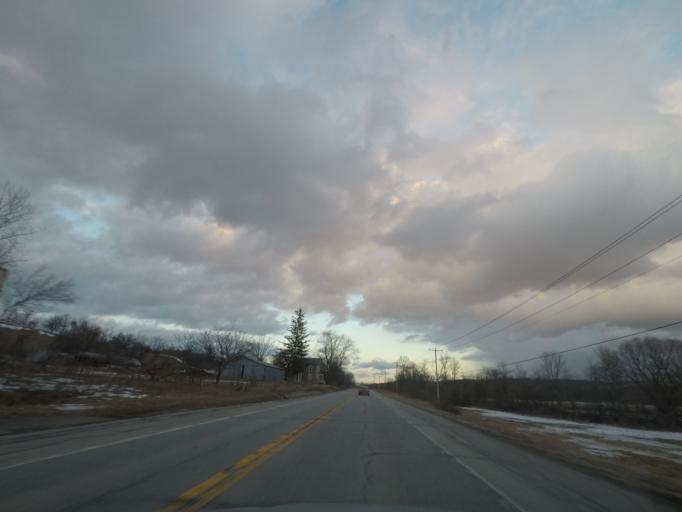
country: US
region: New York
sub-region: Montgomery County
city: Fonda
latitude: 42.9269
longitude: -74.4335
